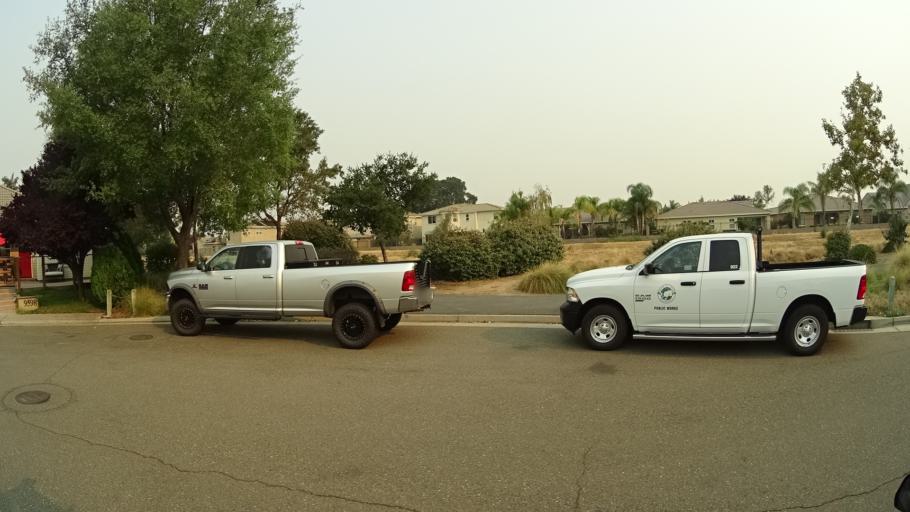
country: US
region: California
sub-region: Sacramento County
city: Laguna
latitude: 38.4049
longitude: -121.4430
